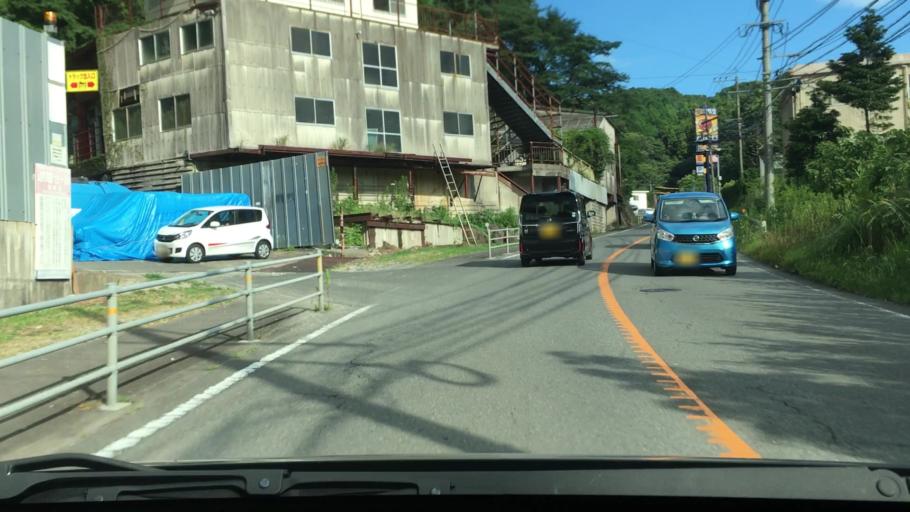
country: JP
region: Nagasaki
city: Togitsu
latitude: 32.8091
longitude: 129.8123
